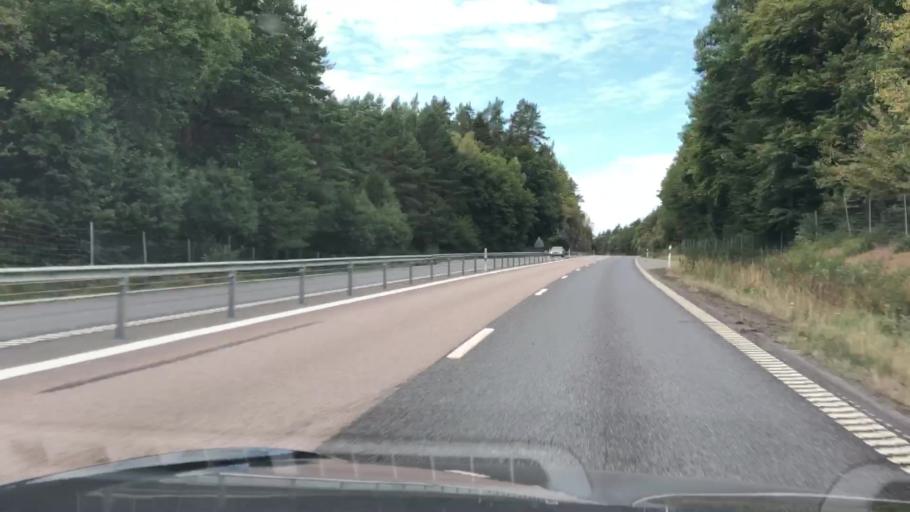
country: SE
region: Blekinge
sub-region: Karlshamns Kommun
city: Karlshamn
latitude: 56.1891
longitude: 14.9005
